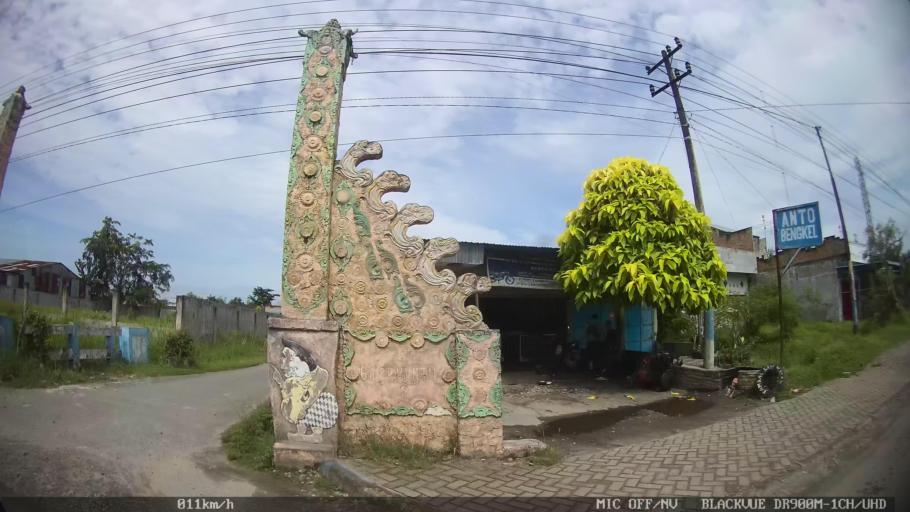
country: ID
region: North Sumatra
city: Percut
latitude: 3.5989
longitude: 98.8074
